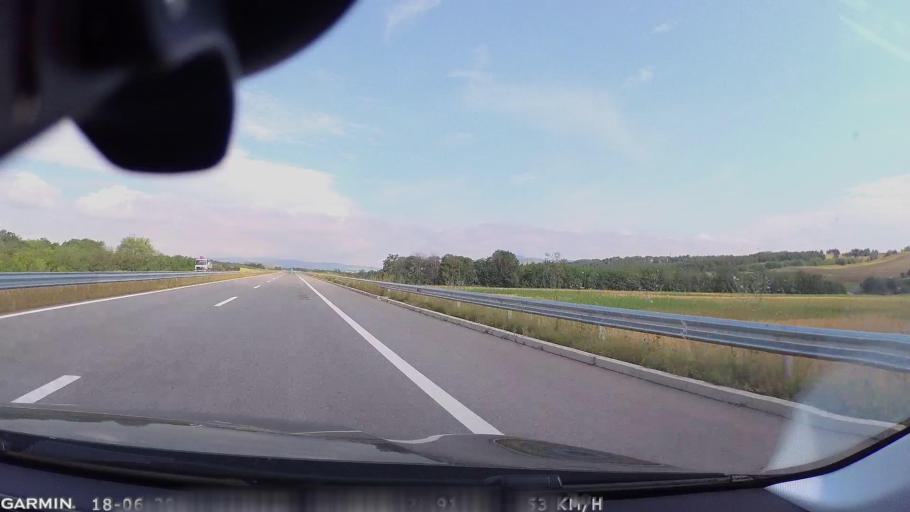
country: MK
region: Sveti Nikole
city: Gorobinci
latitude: 41.9038
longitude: 21.9110
